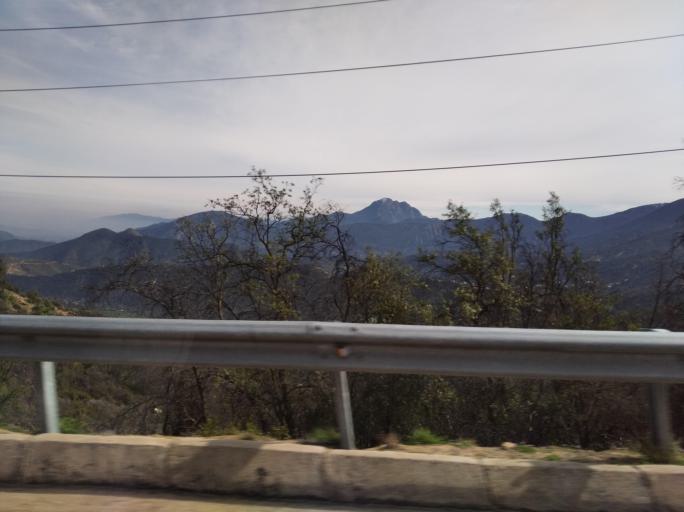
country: CL
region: Valparaiso
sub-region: Provincia de San Felipe
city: Llaillay
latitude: -33.0650
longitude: -71.0138
